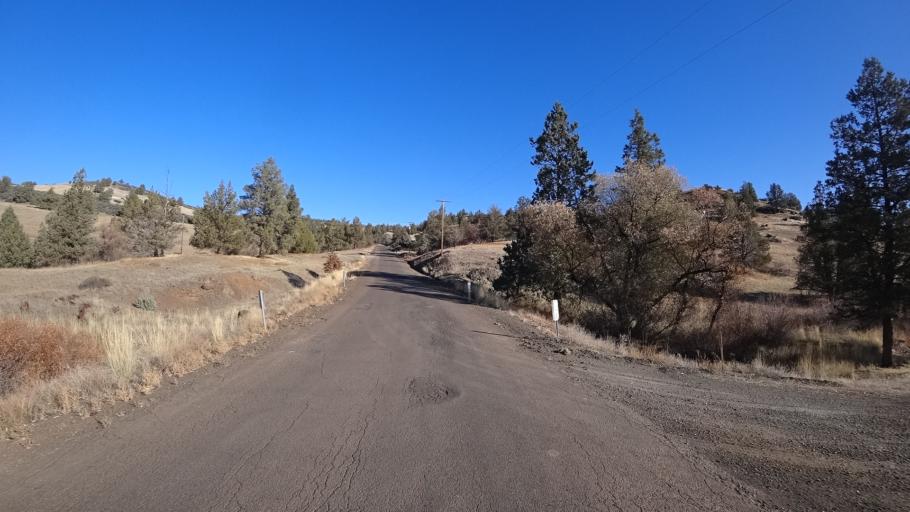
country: US
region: California
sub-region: Siskiyou County
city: Montague
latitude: 41.8949
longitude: -122.4246
